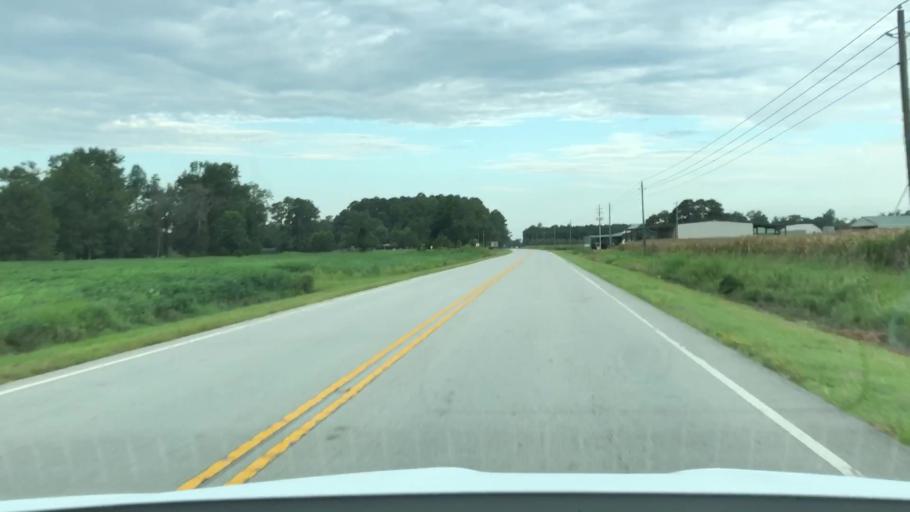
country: US
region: North Carolina
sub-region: Jones County
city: Trenton
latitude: 35.0693
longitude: -77.3702
